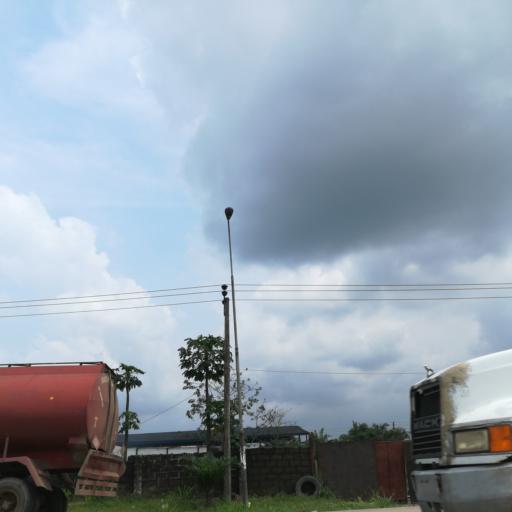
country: NG
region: Rivers
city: Port Harcourt
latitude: 4.8509
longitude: 7.0717
